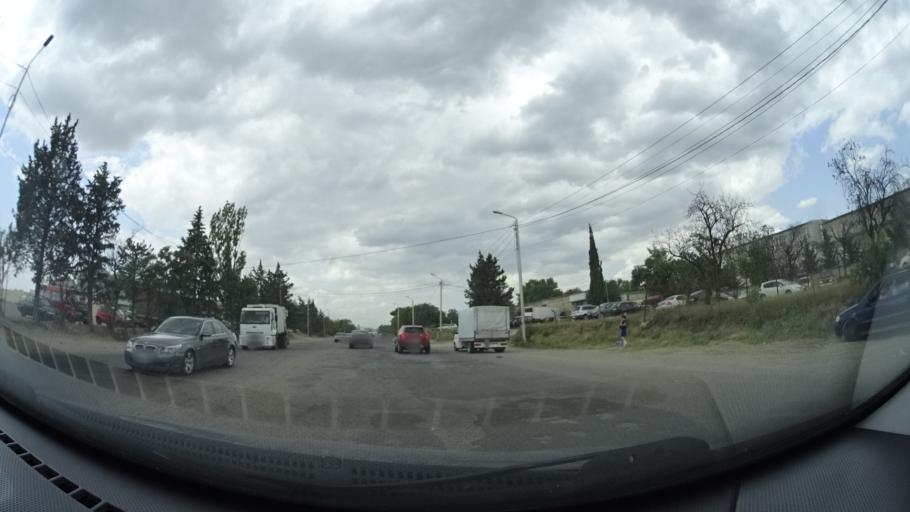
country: GE
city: Didi Lilo
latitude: 41.6915
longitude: 44.9978
